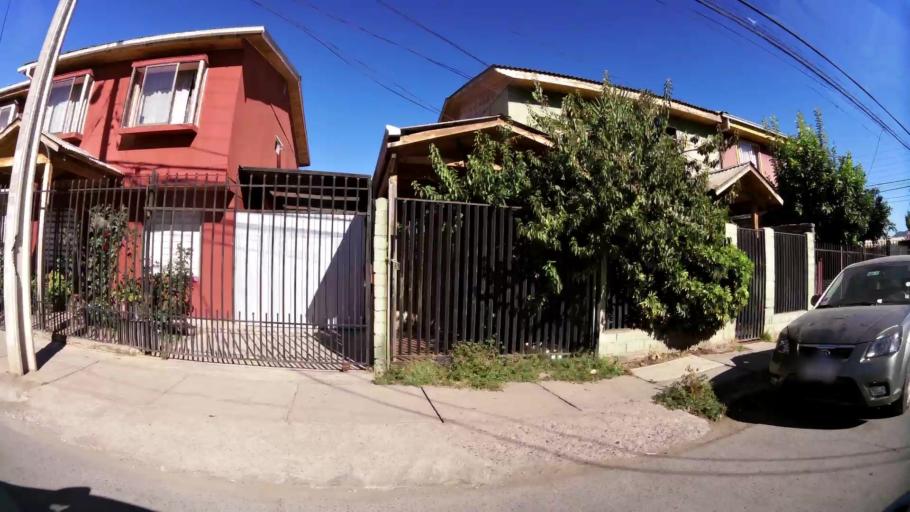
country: CL
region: O'Higgins
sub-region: Provincia de Colchagua
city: Chimbarongo
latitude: -34.5791
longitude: -71.0043
